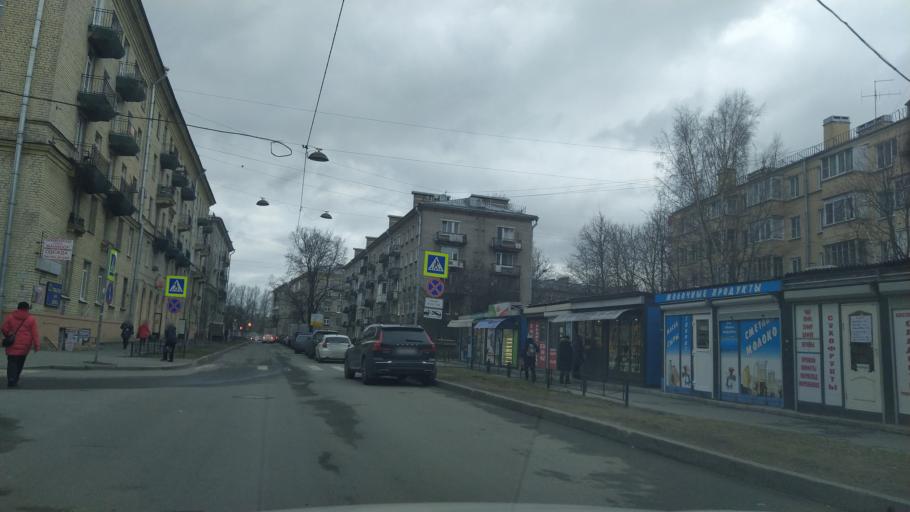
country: RU
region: St.-Petersburg
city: Novaya Derevnya
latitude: 59.9870
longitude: 30.2950
